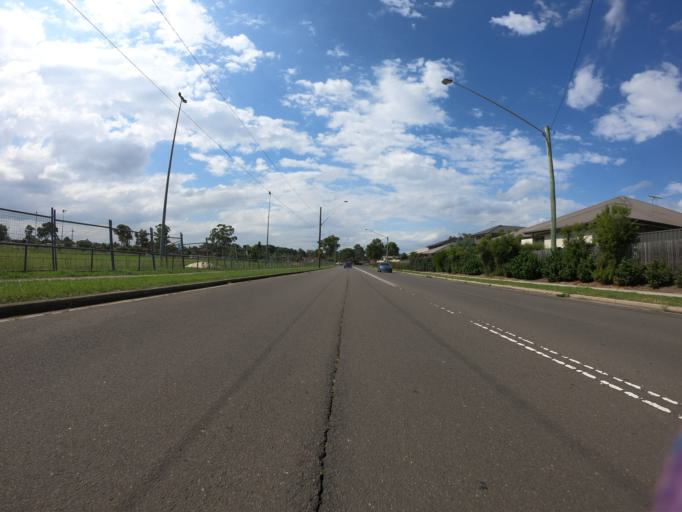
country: AU
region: New South Wales
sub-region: Blacktown
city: Blackett
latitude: -33.7453
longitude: 150.8281
